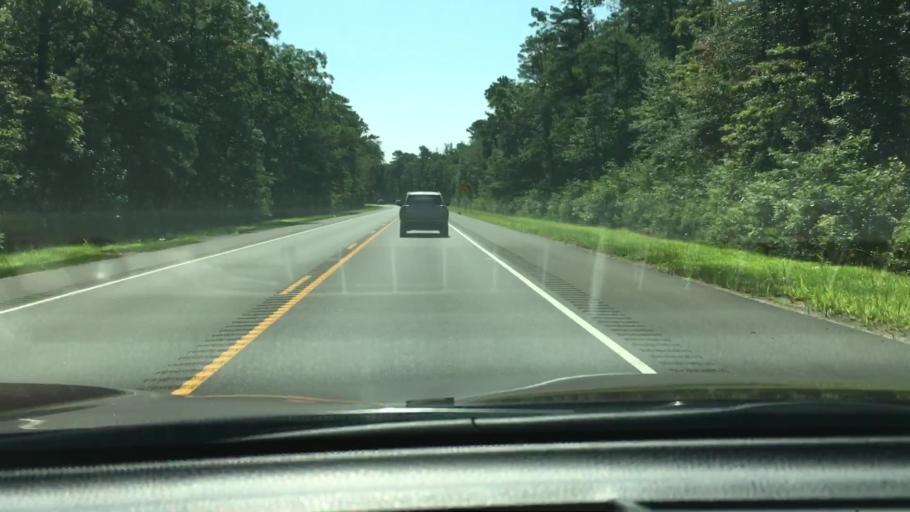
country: US
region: New Jersey
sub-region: Cape May County
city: Woodbine
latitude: 39.3263
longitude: -74.8686
